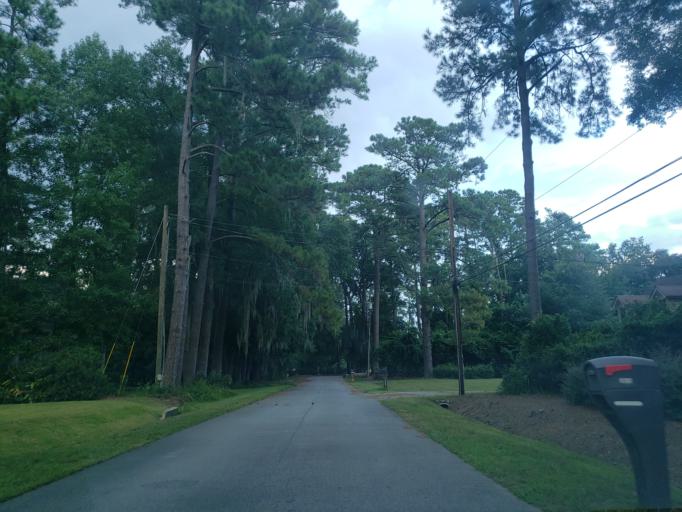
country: US
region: Georgia
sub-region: Chatham County
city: Isle of Hope
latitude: 31.9957
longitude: -81.0610
